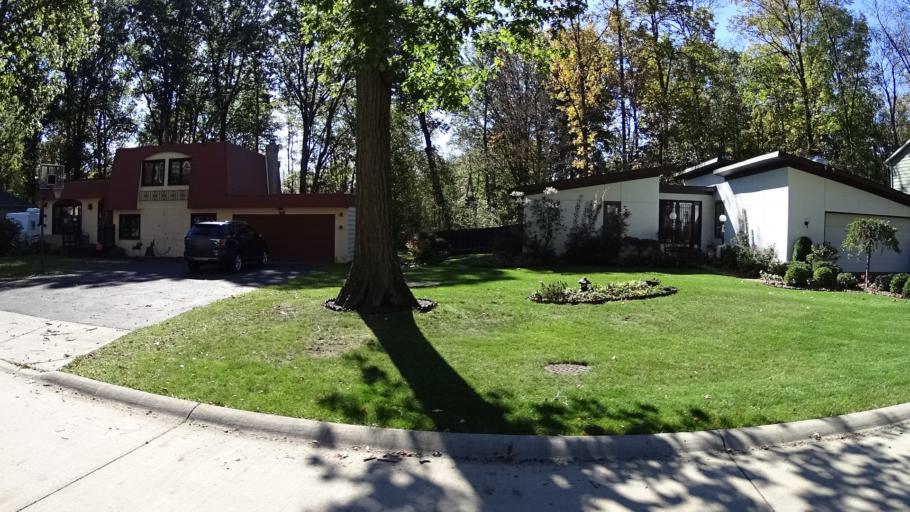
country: US
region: Ohio
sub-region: Lorain County
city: Amherst
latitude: 41.3906
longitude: -82.2475
